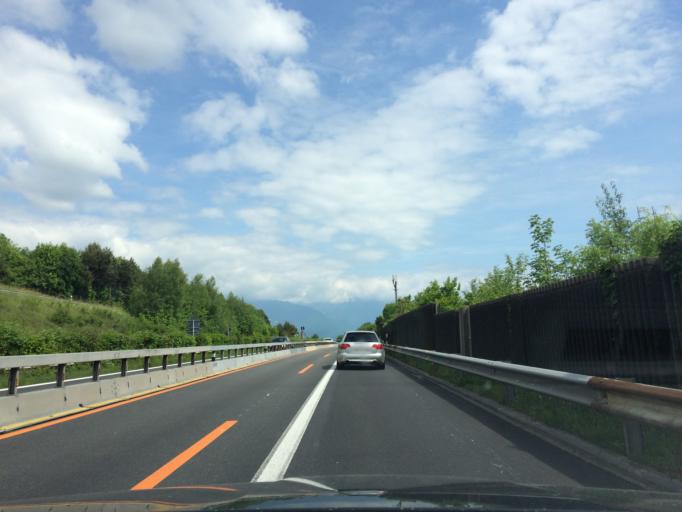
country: CH
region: Vaud
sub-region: Lavaux-Oron District
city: Chexbres
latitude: 46.4846
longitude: 6.7781
